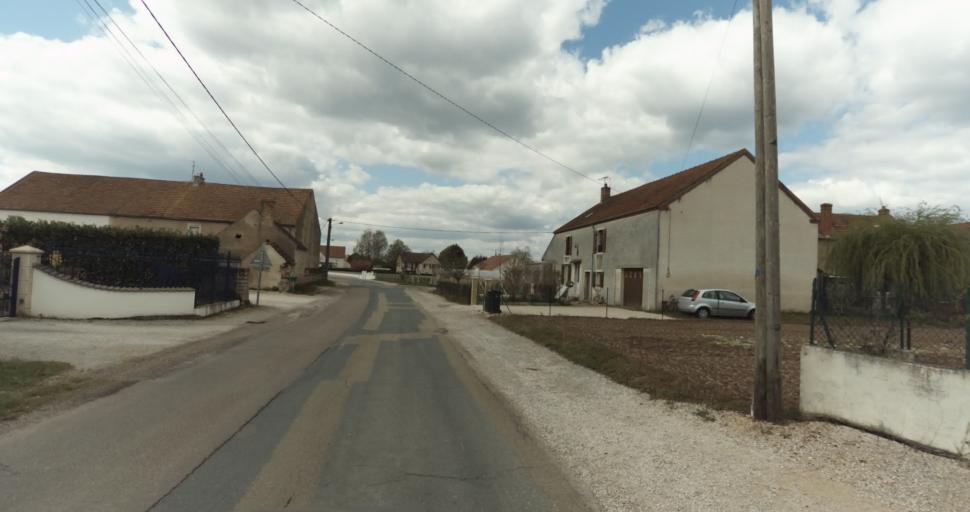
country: FR
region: Bourgogne
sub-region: Departement de la Cote-d'Or
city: Auxonne
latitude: 47.1890
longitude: 5.4013
